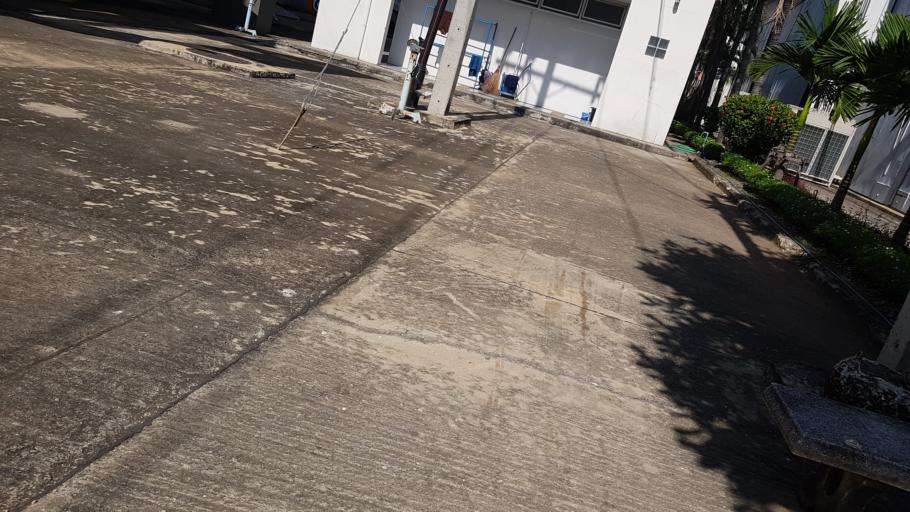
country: TH
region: Bangkok
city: Sai Mai
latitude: 13.9195
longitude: 100.6215
